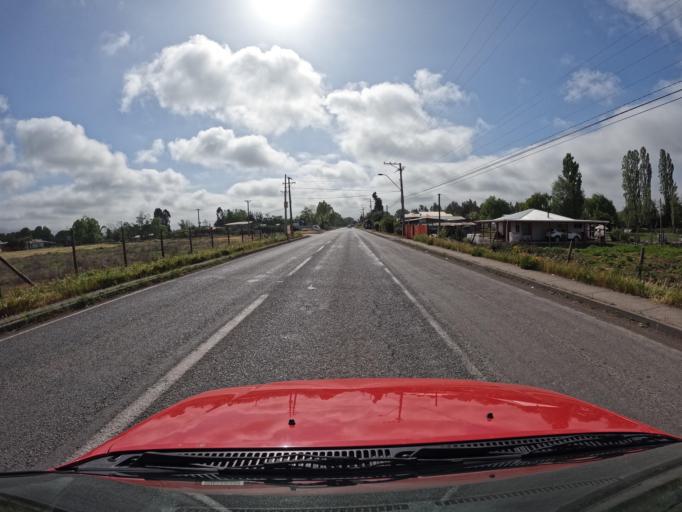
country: CL
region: Maule
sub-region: Provincia de Curico
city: Teno
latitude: -34.8600
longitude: -71.1919
